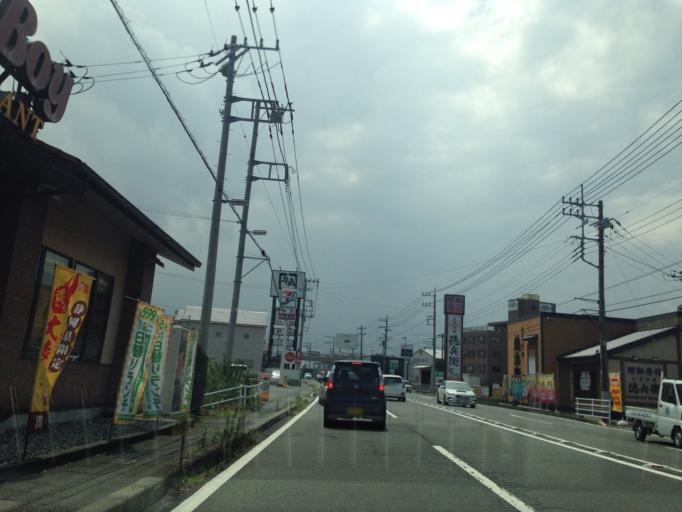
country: JP
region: Shizuoka
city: Mishima
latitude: 35.1085
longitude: 138.9201
